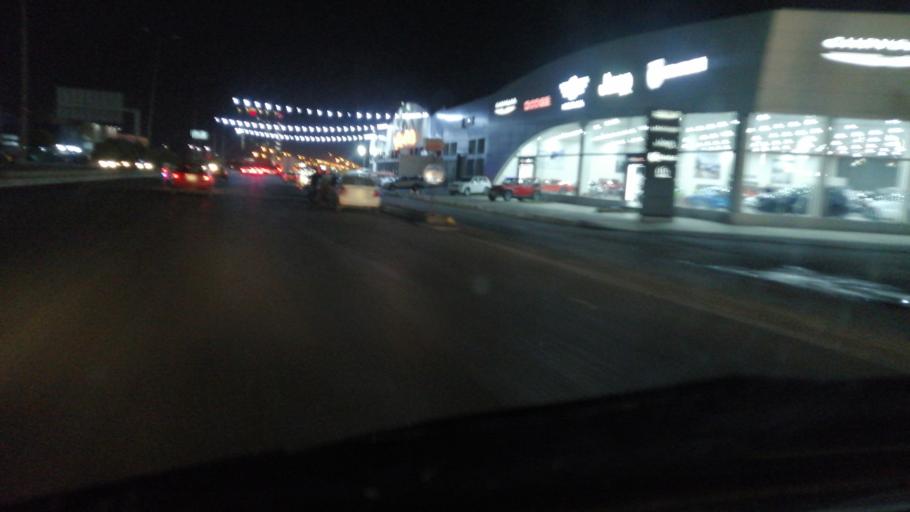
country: IQ
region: Arbil
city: Erbil
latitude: 36.1570
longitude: 43.9888
